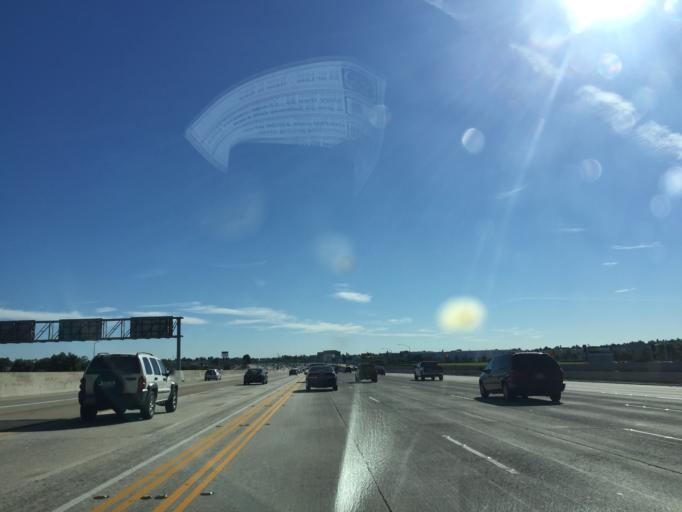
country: US
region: California
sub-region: Orange County
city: Laguna Woods
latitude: 33.6389
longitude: -117.7307
